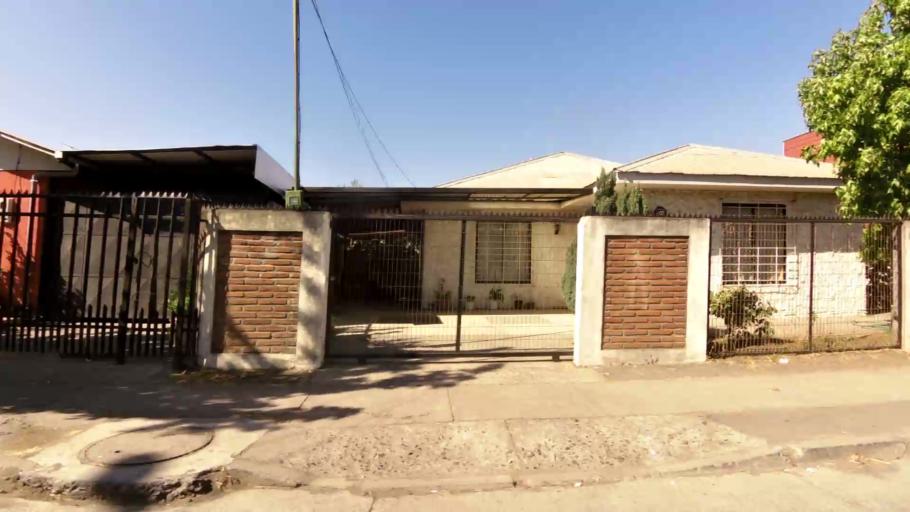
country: CL
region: Maule
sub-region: Provincia de Curico
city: Curico
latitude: -34.9816
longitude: -71.2547
